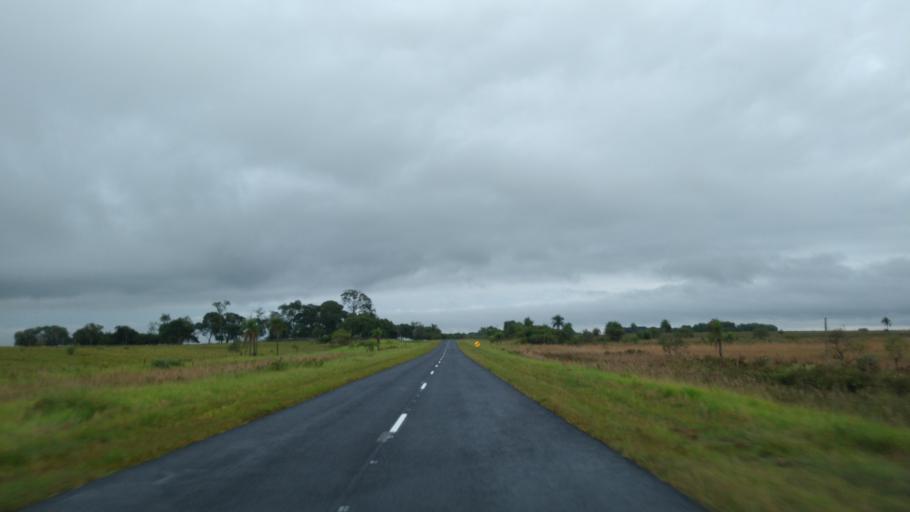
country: AR
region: Corrientes
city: Loreto
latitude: -27.7115
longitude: -57.2286
